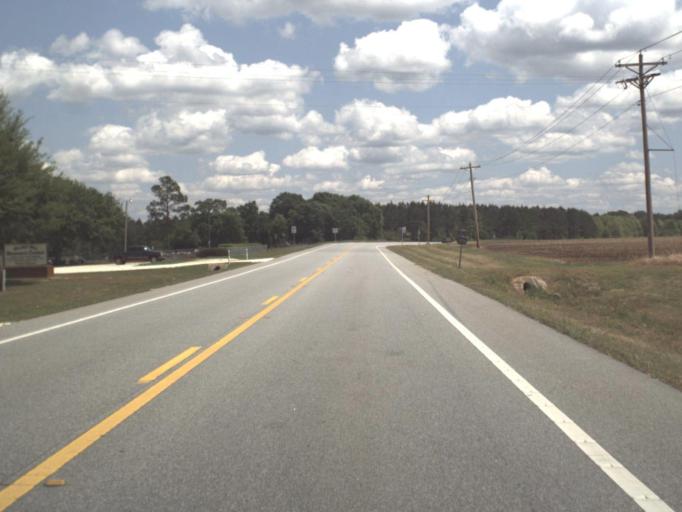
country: US
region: Alabama
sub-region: Escambia County
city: Atmore
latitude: 30.8860
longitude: -87.4534
